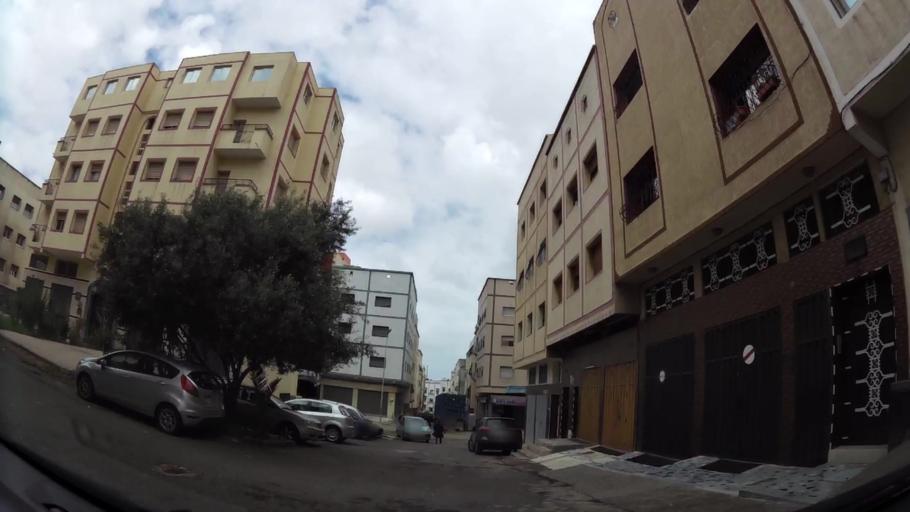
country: MA
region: Grand Casablanca
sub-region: Casablanca
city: Casablanca
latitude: 33.5352
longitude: -7.5869
